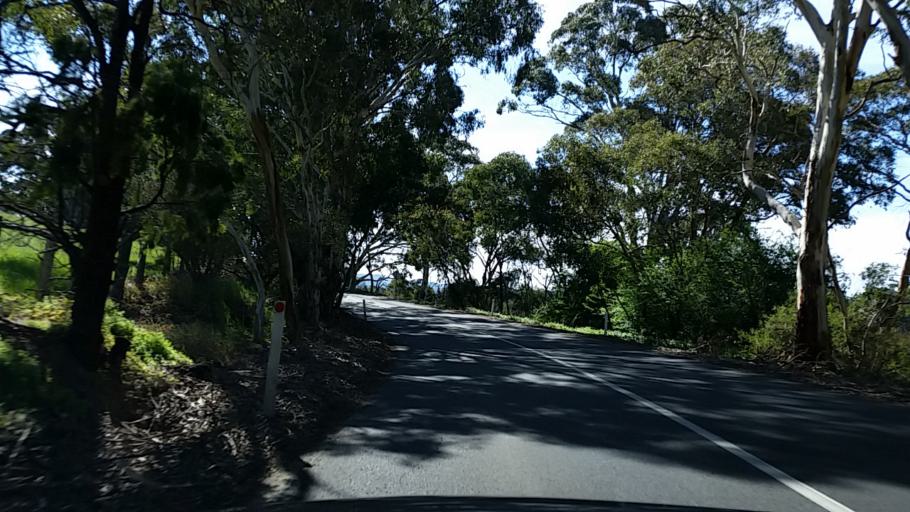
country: AU
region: South Australia
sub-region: Mount Barker
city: Little Hampton
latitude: -35.0762
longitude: 138.8189
